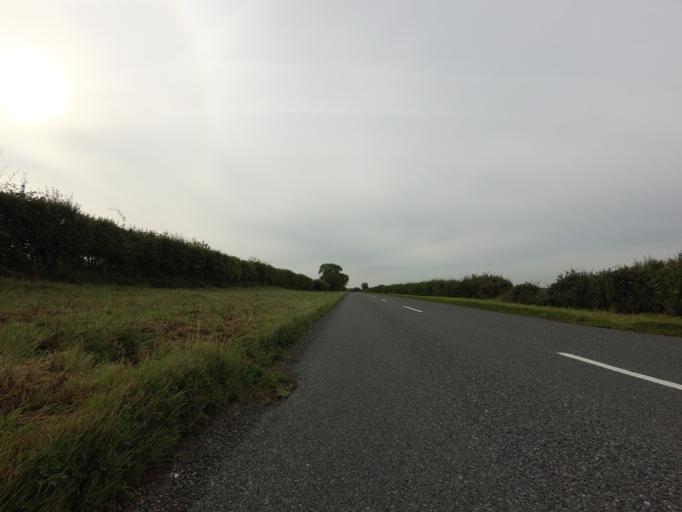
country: GB
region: England
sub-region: Cambridgeshire
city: Melbourn
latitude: 52.0492
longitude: 0.0461
